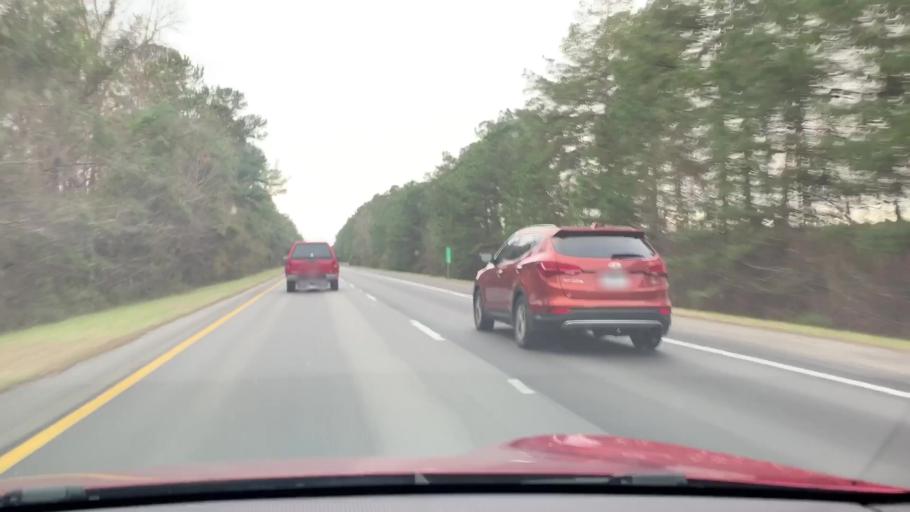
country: US
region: South Carolina
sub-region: Clarendon County
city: Manning
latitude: 33.6334
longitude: -80.2899
